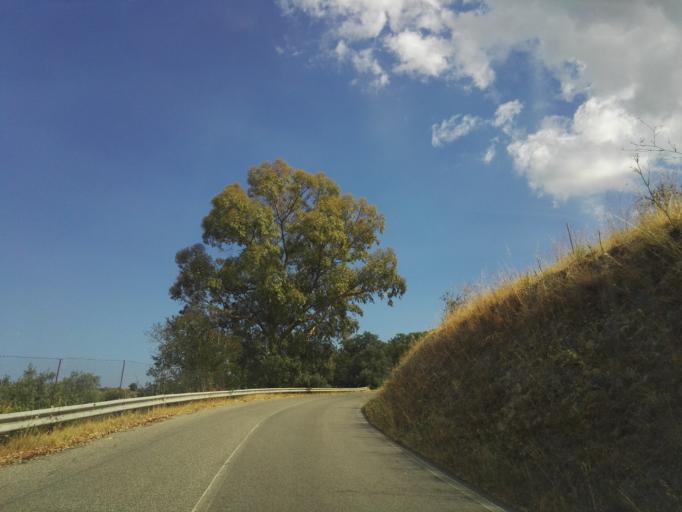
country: IT
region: Calabria
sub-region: Provincia di Reggio Calabria
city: Camini
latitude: 38.4263
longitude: 16.4868
